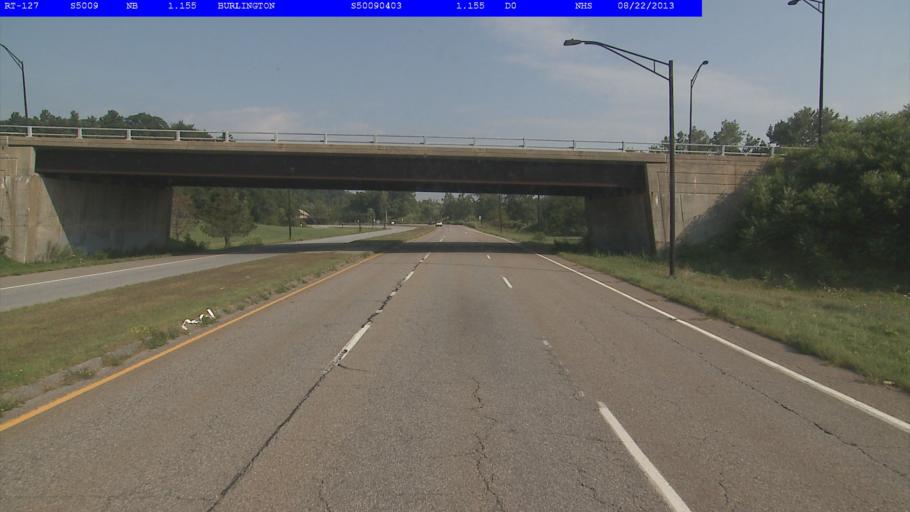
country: US
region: Vermont
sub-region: Chittenden County
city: Burlington
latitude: 44.5018
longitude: -73.2306
